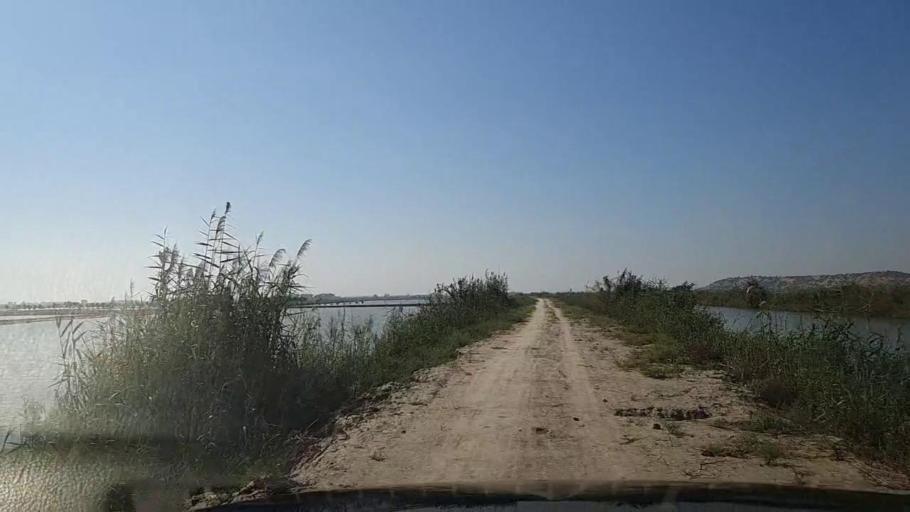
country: PK
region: Sindh
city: Thatta
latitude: 24.6832
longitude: 67.8914
